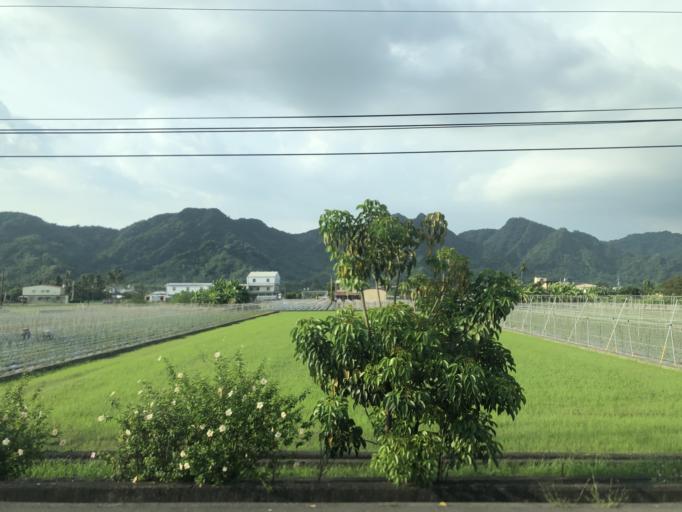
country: TW
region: Taiwan
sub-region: Pingtung
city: Pingtung
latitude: 22.8857
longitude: 120.5108
